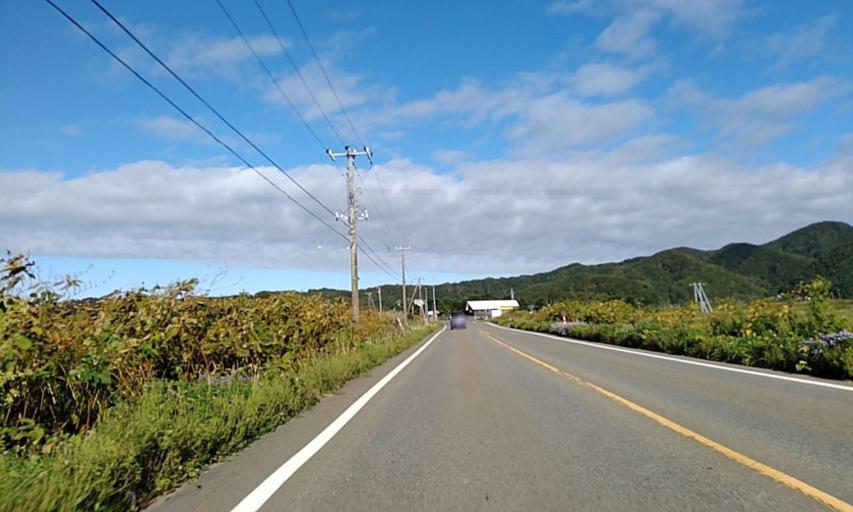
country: JP
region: Hokkaido
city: Shizunai-furukawacho
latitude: 42.2675
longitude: 142.5106
